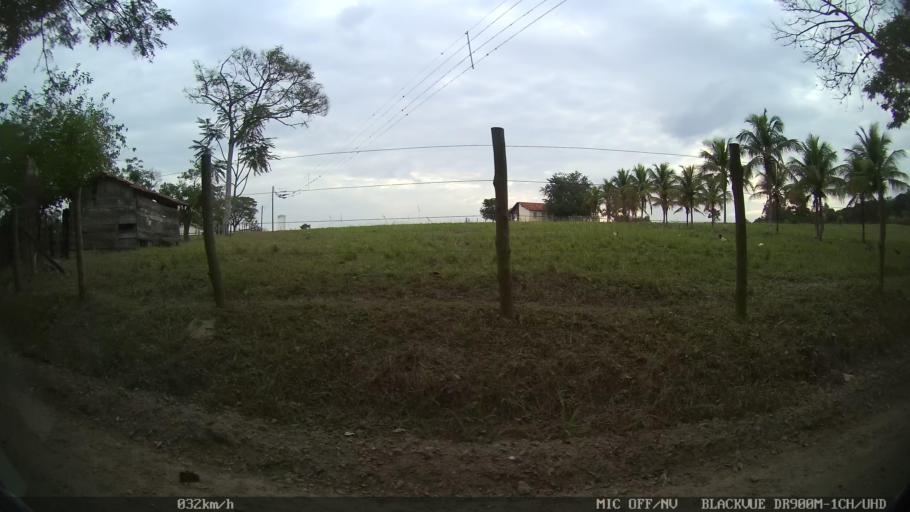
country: BR
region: Sao Paulo
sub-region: Americana
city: Americana
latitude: -22.6767
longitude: -47.3729
